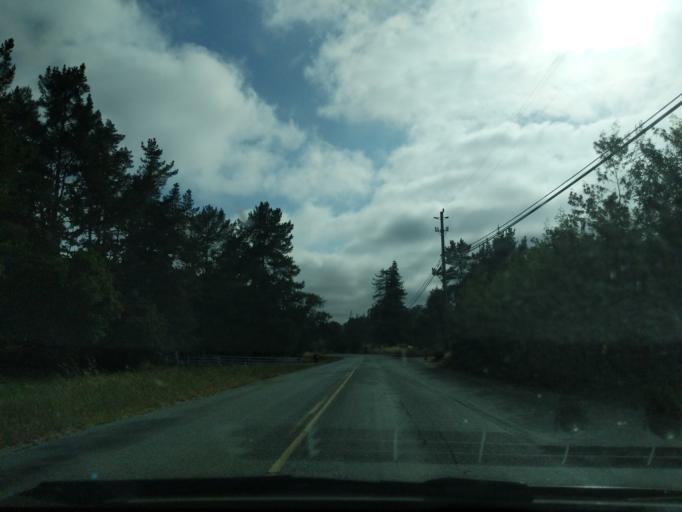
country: US
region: California
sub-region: Monterey County
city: Prunedale
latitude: 36.7965
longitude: -121.6546
